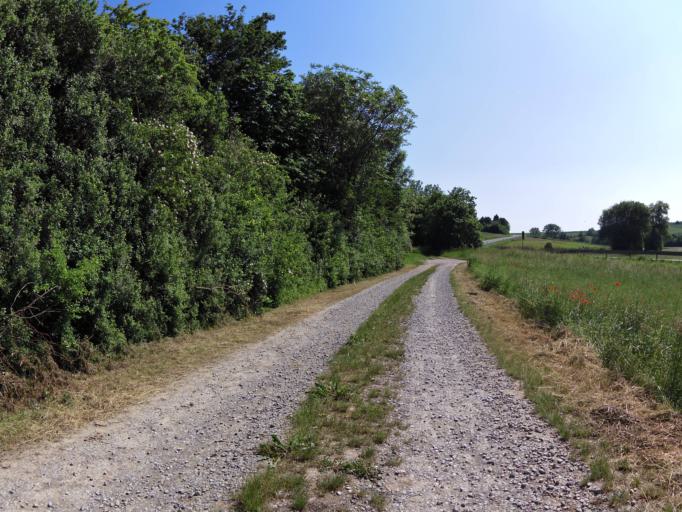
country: DE
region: Bavaria
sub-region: Regierungsbezirk Unterfranken
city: Kleinrinderfeld
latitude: 49.7084
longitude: 9.8422
